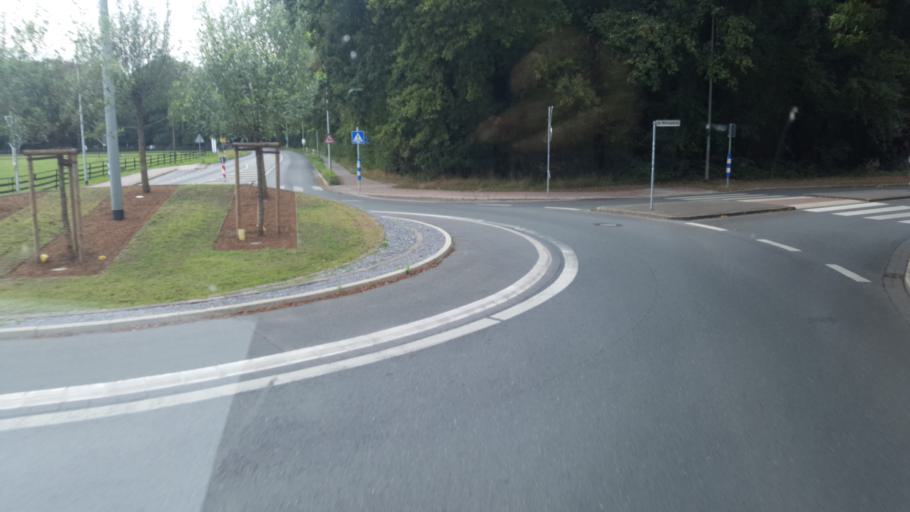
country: DE
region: North Rhine-Westphalia
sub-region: Regierungsbezirk Dusseldorf
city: Dinslaken
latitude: 51.5716
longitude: 6.7156
